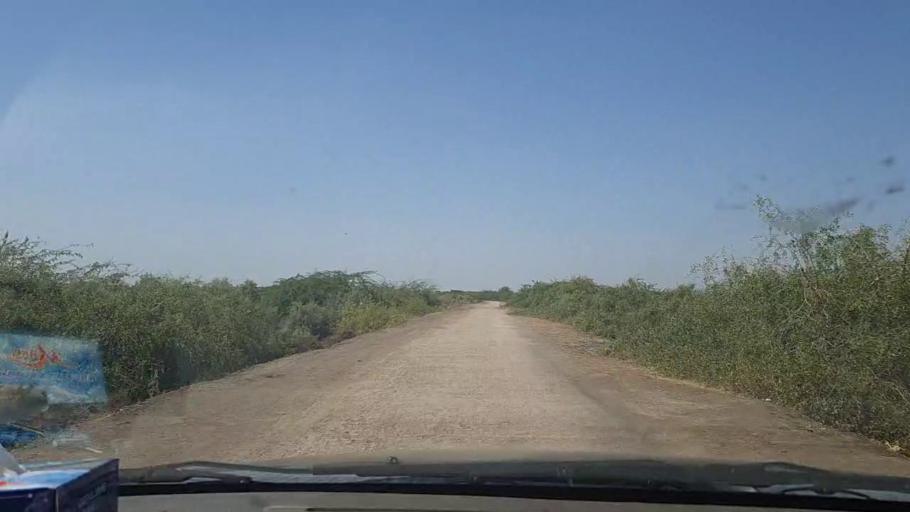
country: PK
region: Sindh
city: Chuhar Jamali
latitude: 24.2794
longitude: 67.7625
